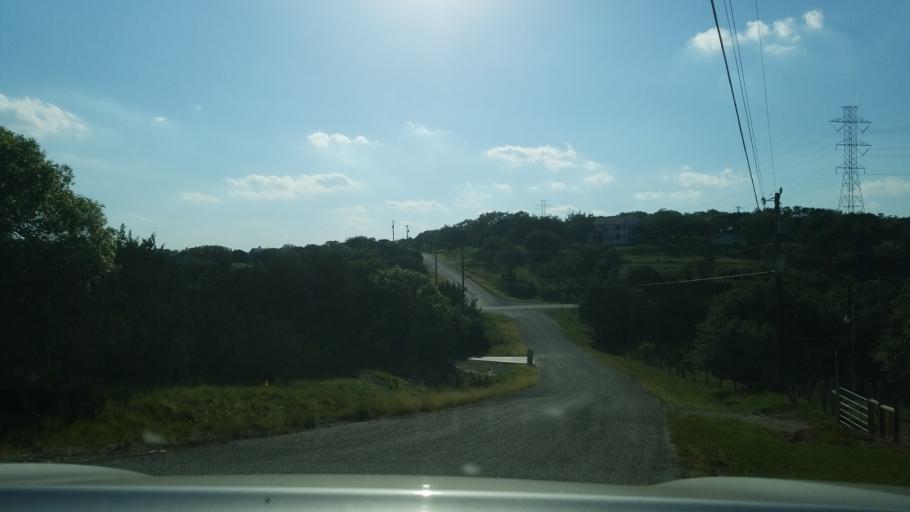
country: US
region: Texas
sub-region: Comal County
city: Bulverde
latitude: 29.7773
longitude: -98.4293
